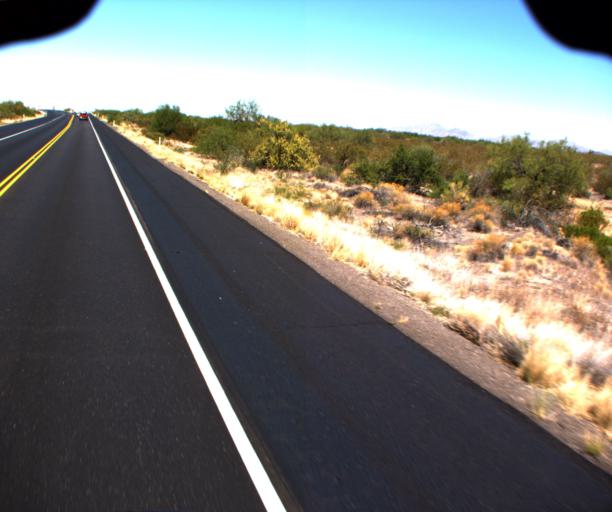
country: US
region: Arizona
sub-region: Yavapai County
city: Congress
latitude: 34.0533
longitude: -112.8498
